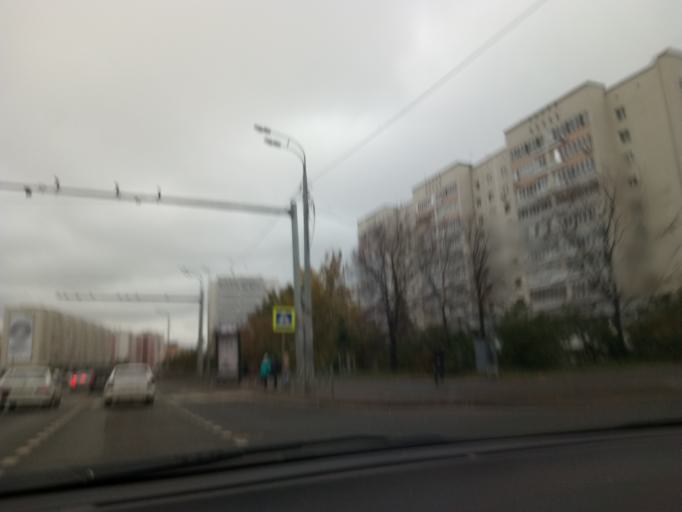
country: RU
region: Tatarstan
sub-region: Gorod Kazan'
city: Kazan
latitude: 55.7881
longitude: 49.1515
